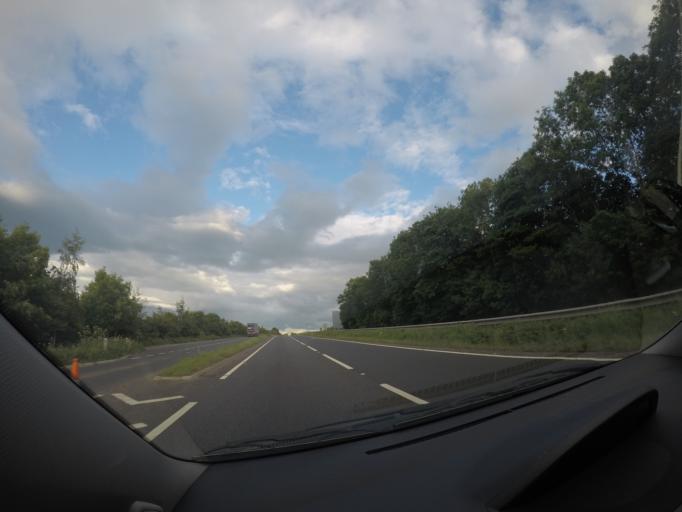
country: GB
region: England
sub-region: County Durham
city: Rokeby
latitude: 54.5076
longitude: -1.8518
